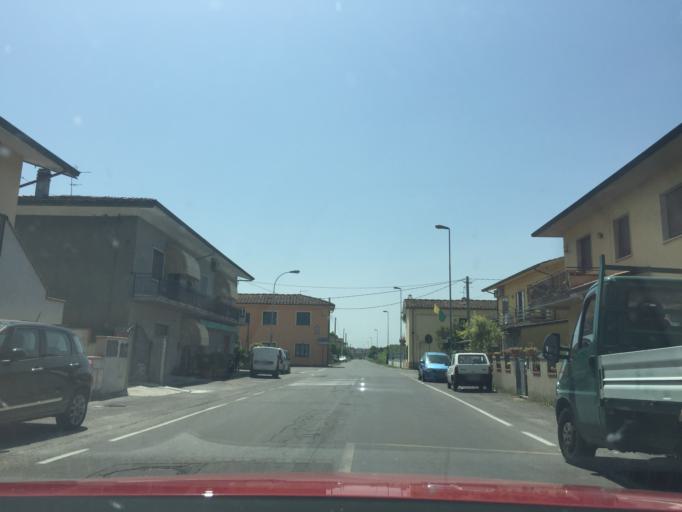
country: IT
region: Tuscany
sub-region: Provincia di Pistoia
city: Anchione
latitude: 43.8303
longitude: 10.7548
